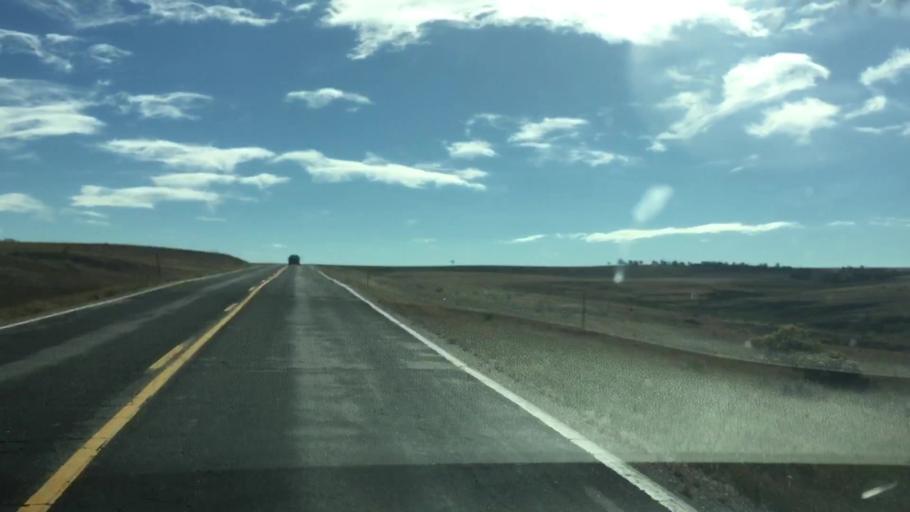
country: US
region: Colorado
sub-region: Elbert County
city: Kiowa
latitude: 39.2751
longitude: -104.2552
